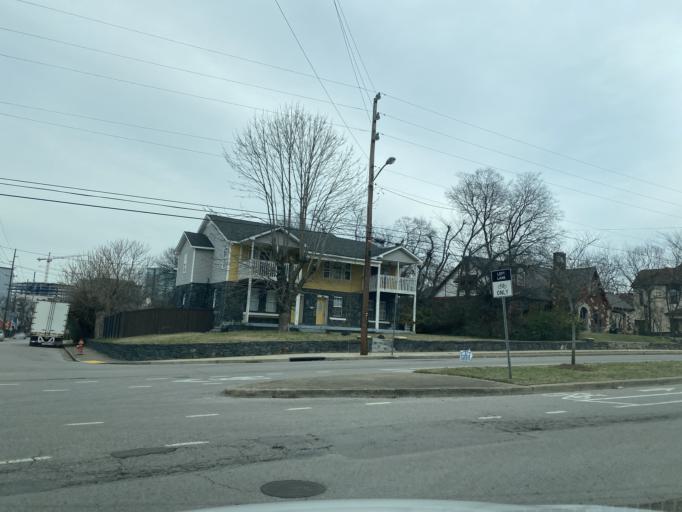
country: US
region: Tennessee
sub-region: Davidson County
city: Nashville
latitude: 36.1476
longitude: -86.7888
